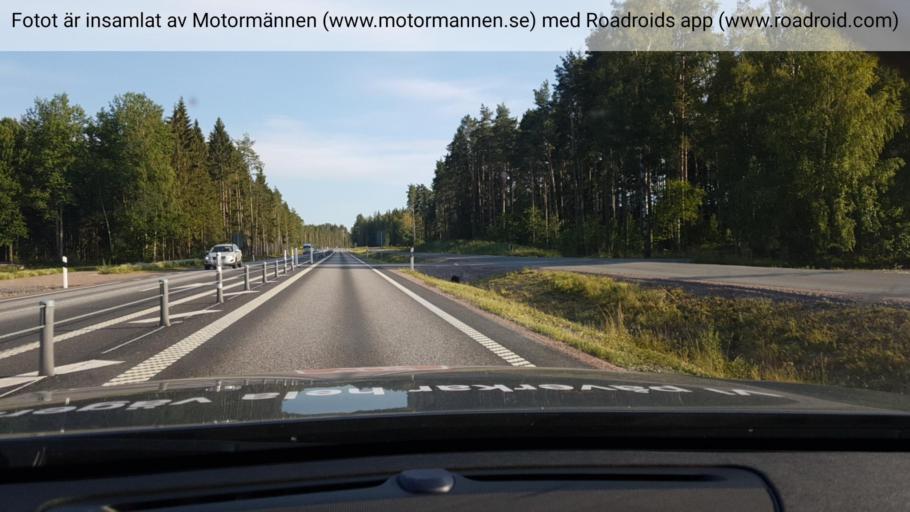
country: SE
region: Uppsala
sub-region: Osthammars Kommun
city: Gimo
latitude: 60.1049
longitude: 18.1246
